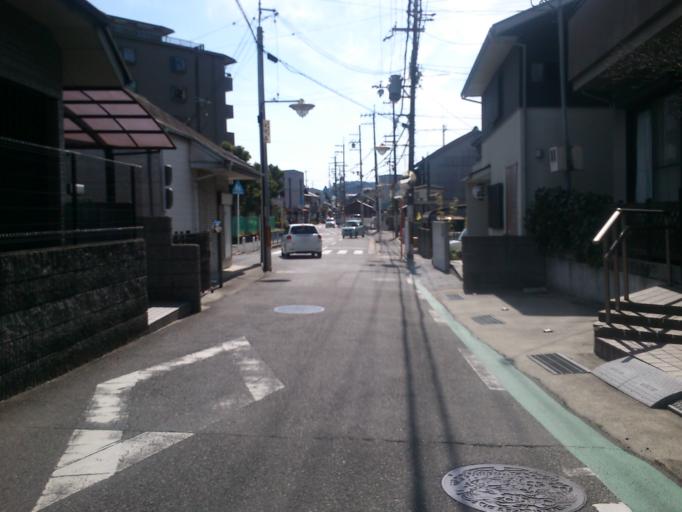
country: JP
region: Kyoto
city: Yawata
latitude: 34.8902
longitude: 135.6739
